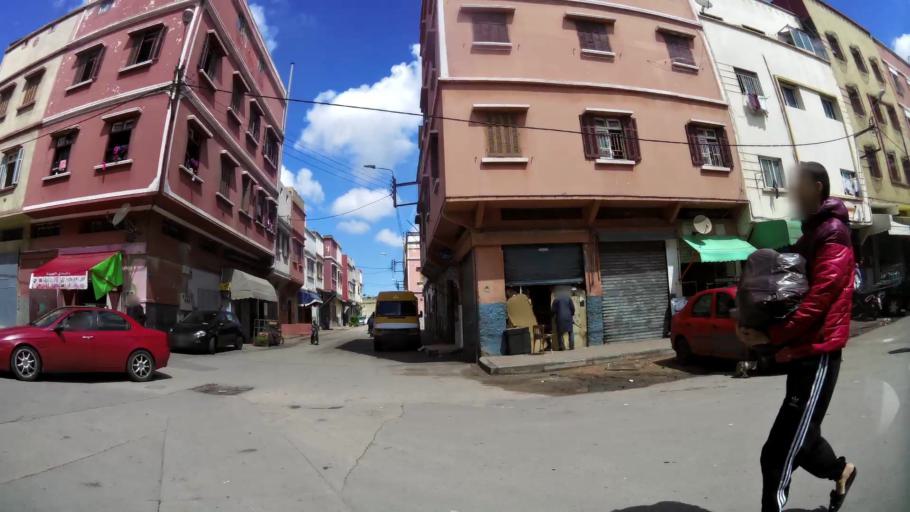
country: MA
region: Grand Casablanca
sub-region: Casablanca
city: Casablanca
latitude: 33.5585
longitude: -7.6043
